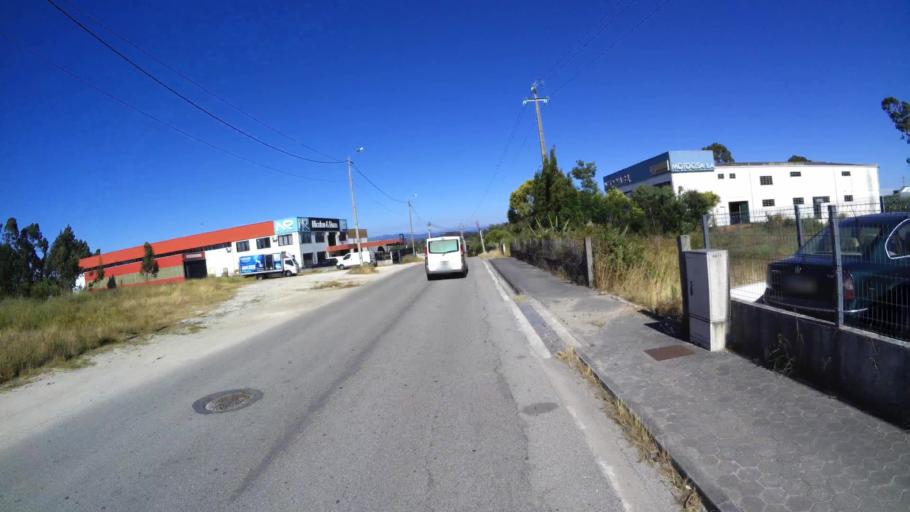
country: PT
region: Aveiro
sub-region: Aveiro
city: Eixo
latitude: 40.6511
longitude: -8.6009
